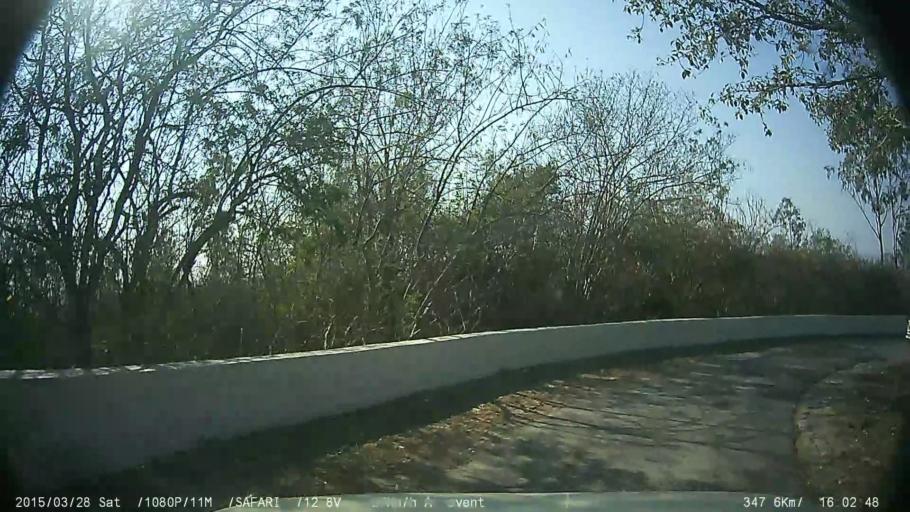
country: IN
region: Karnataka
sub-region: Mysore
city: Mysore
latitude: 12.2798
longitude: 76.6673
